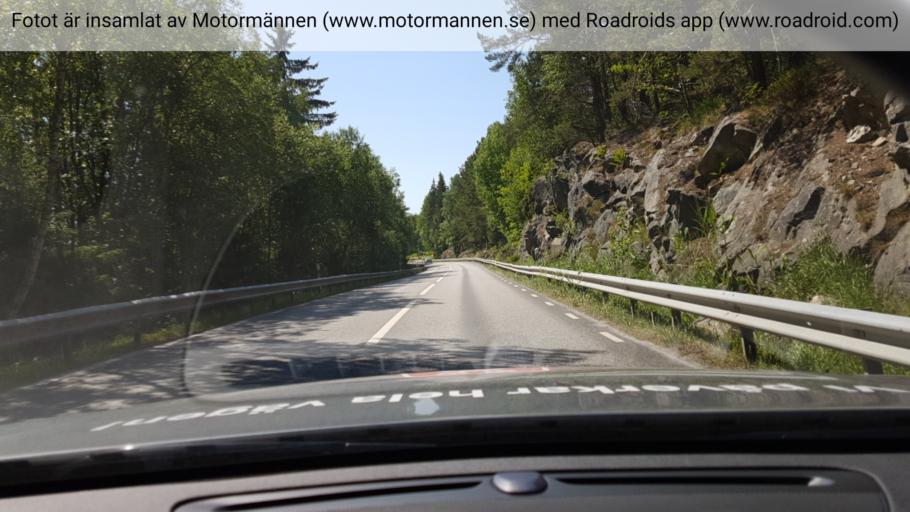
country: SE
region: Stockholm
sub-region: Norrtalje Kommun
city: Rimbo
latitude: 59.6628
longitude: 18.3449
